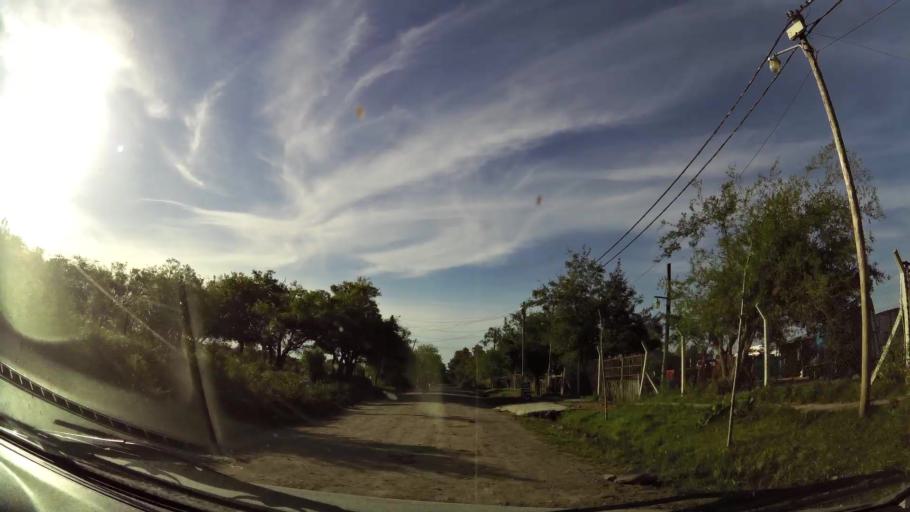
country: AR
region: Buenos Aires
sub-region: Partido de Almirante Brown
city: Adrogue
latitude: -34.8194
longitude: -58.3286
